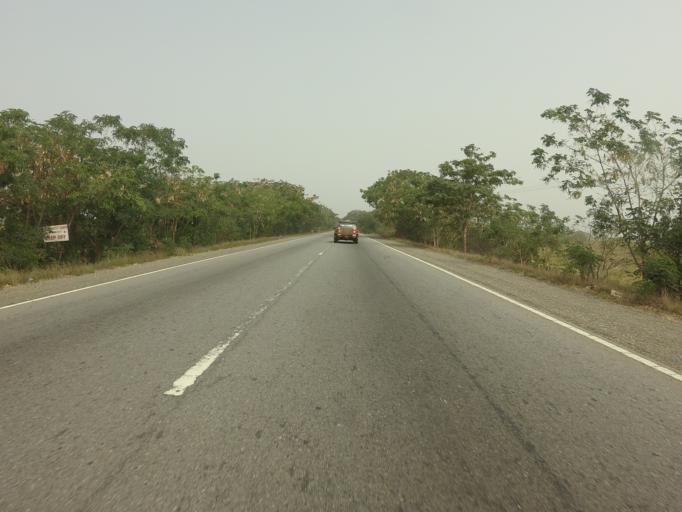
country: GH
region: Volta
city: Anloga
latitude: 5.8882
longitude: 0.4603
